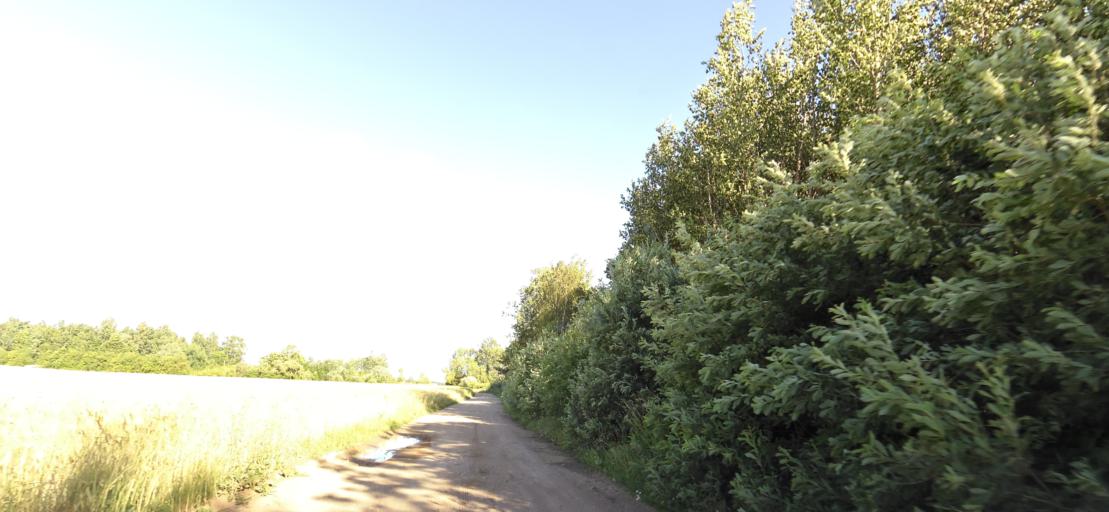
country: LT
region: Panevezys
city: Pasvalys
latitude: 56.1300
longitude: 24.5534
